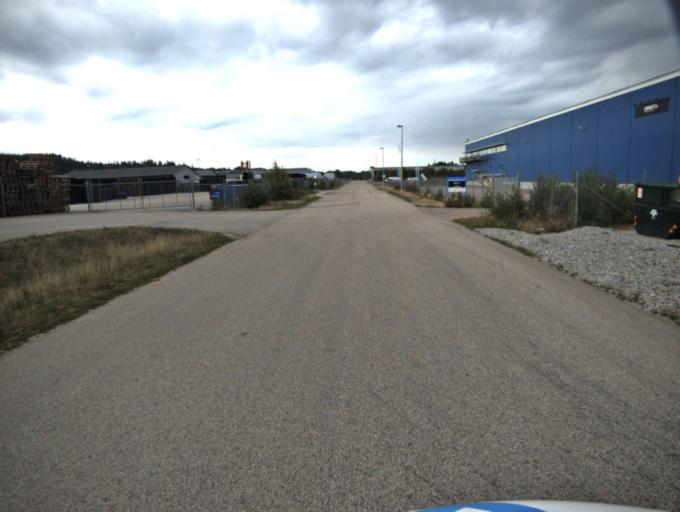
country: SE
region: Vaestra Goetaland
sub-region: Ulricehamns Kommun
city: Ulricehamn
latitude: 57.8357
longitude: 13.4228
